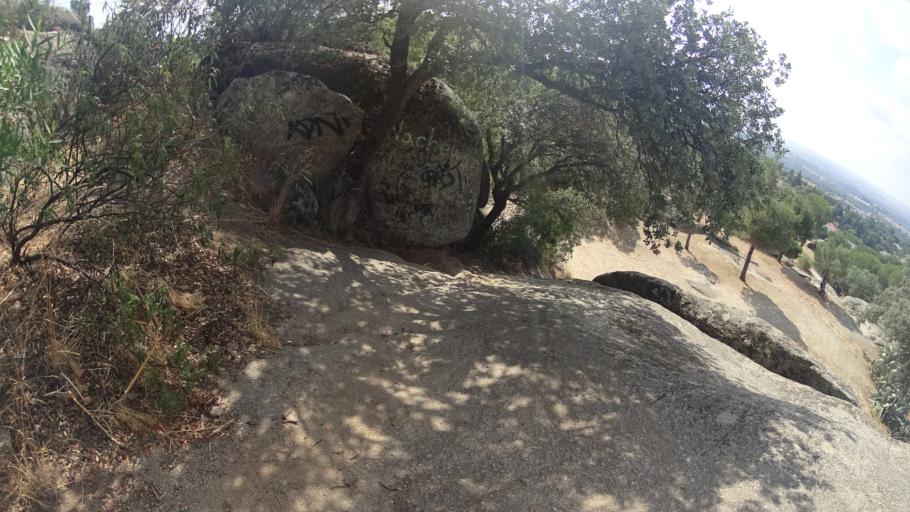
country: ES
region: Madrid
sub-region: Provincia de Madrid
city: Torrelodones
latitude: 40.5879
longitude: -3.9213
